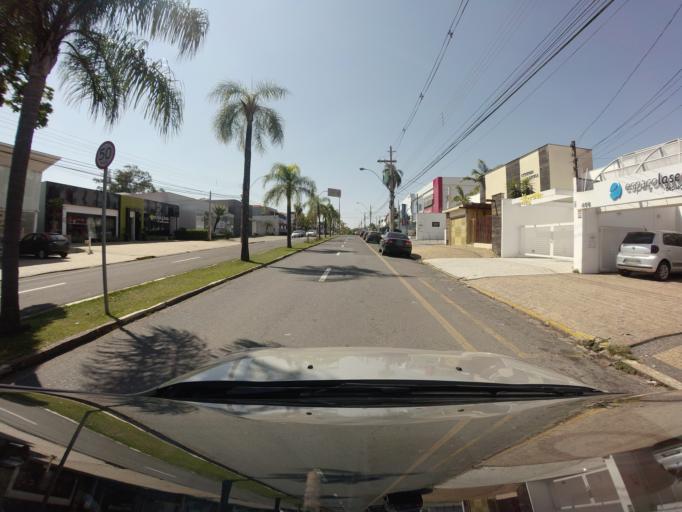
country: BR
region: Sao Paulo
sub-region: Piracicaba
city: Piracicaba
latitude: -22.7163
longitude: -47.6384
